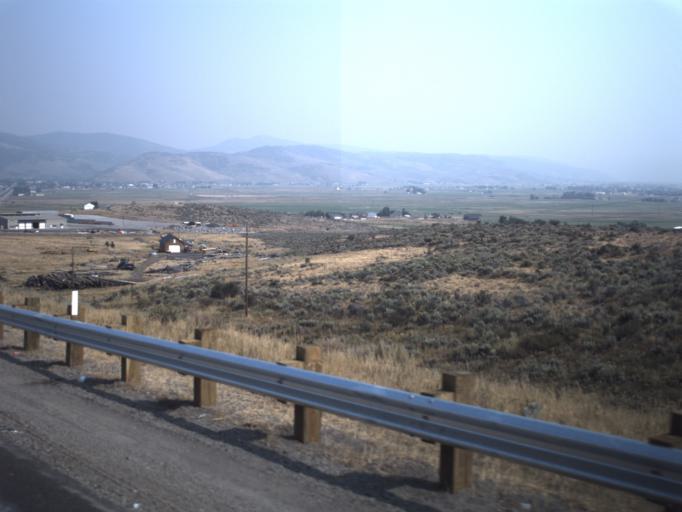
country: US
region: Utah
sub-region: Summit County
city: Kamas
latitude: 40.6391
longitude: -111.3267
